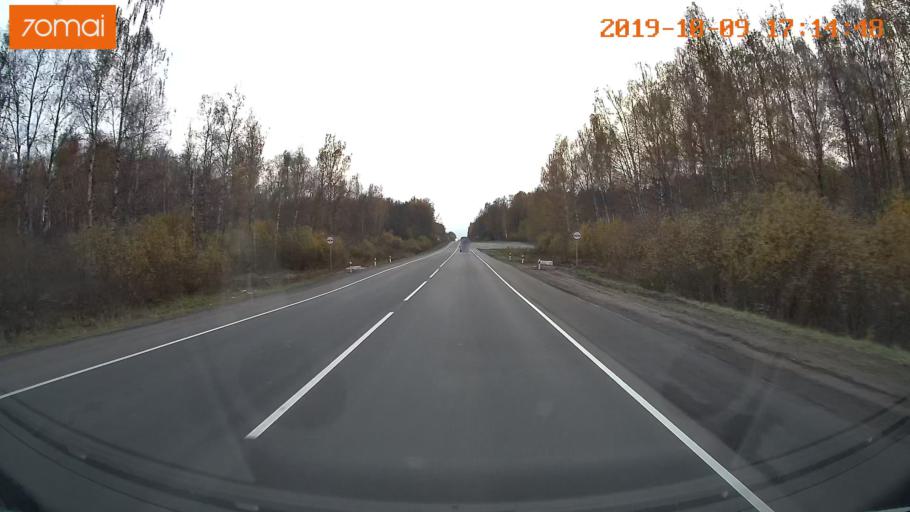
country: RU
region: Ivanovo
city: Furmanov
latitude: 57.3028
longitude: 41.2040
